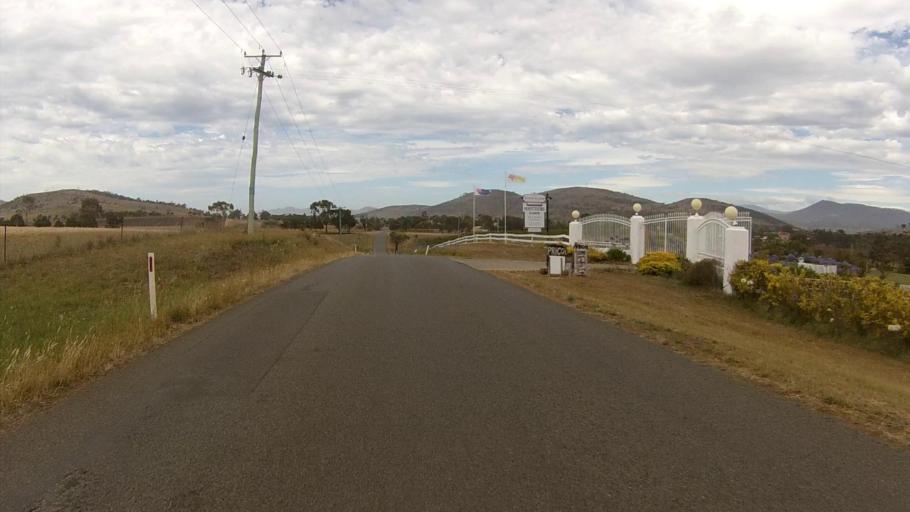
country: AU
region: Tasmania
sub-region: Clarence
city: Cambridge
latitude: -42.7265
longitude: 147.4496
